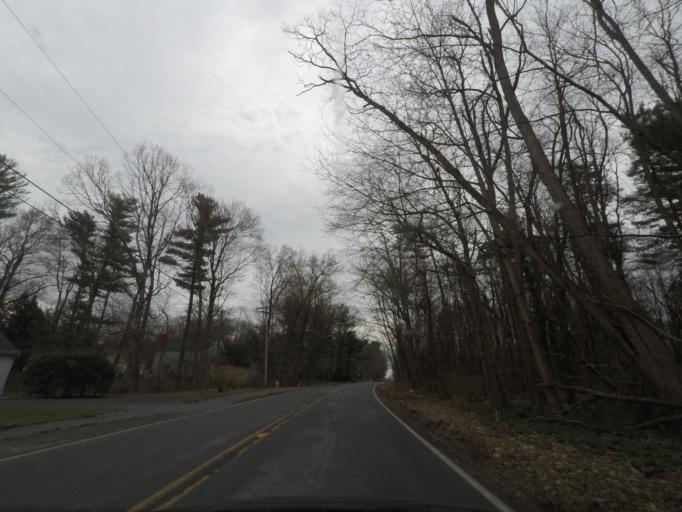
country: US
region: New York
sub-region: Albany County
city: Delmar
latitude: 42.6023
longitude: -73.8285
